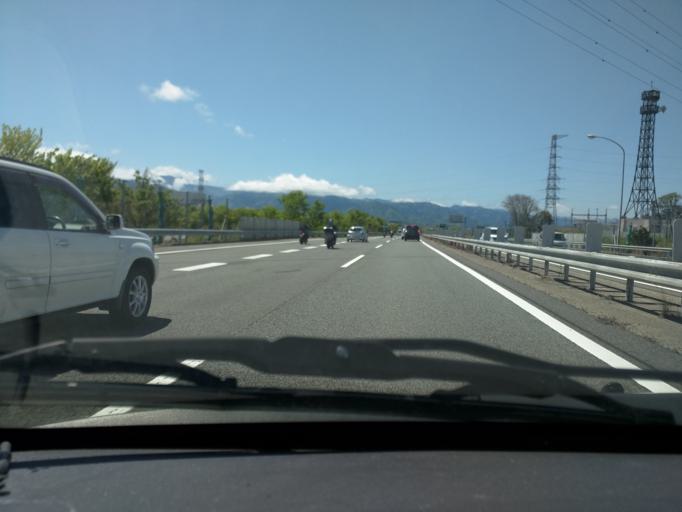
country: JP
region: Nagano
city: Nakano
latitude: 36.7284
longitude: 138.3169
